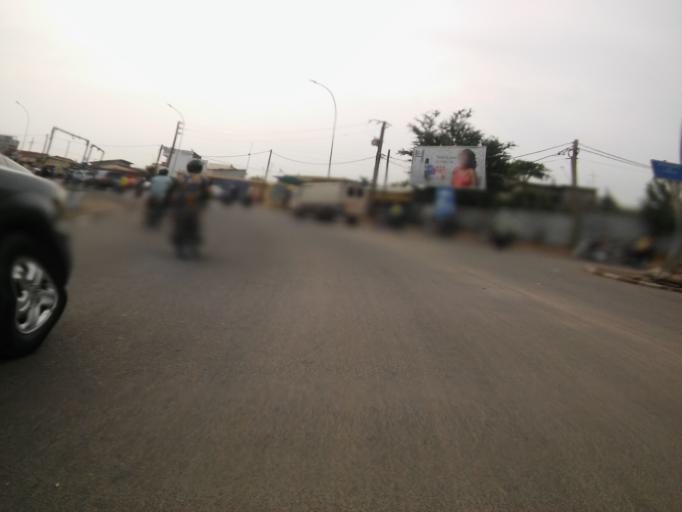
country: BJ
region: Littoral
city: Cotonou
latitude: 6.3712
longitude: 2.4091
